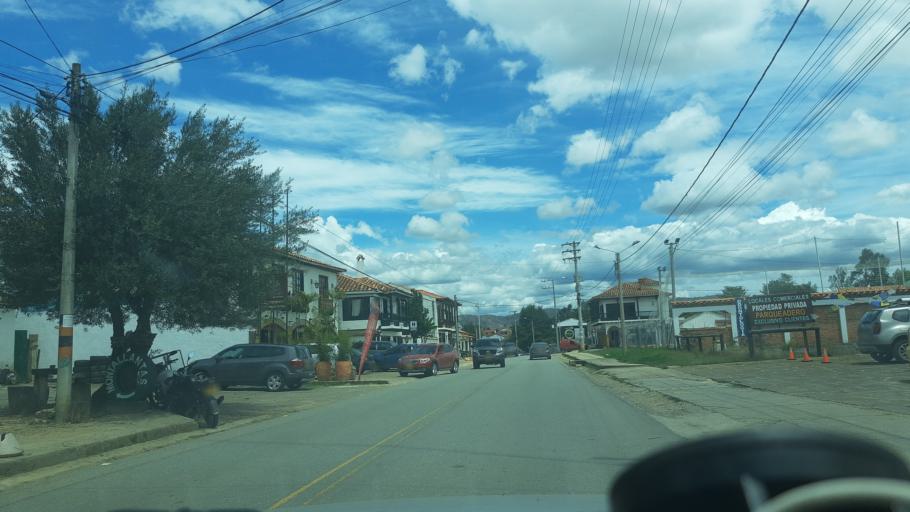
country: CO
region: Boyaca
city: Villa de Leiva
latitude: 5.6279
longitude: -73.5289
